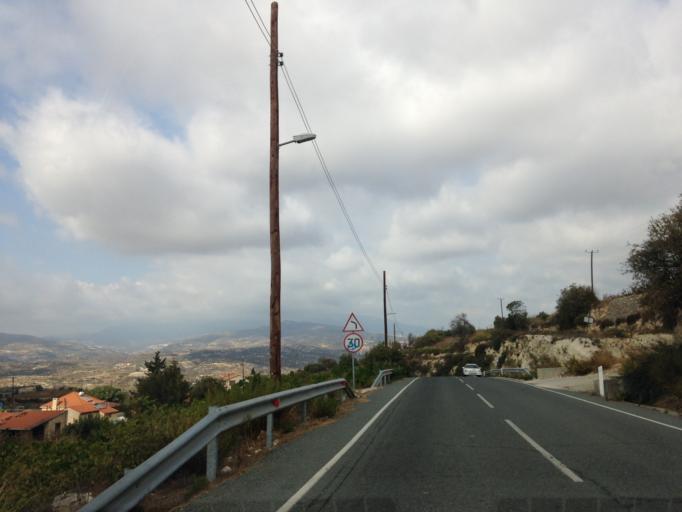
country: CY
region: Limassol
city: Pachna
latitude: 34.7770
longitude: 32.7971
